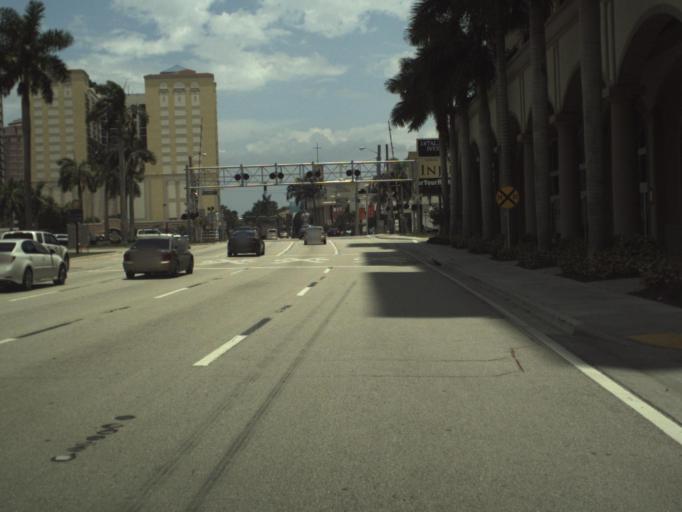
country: US
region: Florida
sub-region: Palm Beach County
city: West Palm Beach
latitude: 26.7056
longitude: -80.0565
